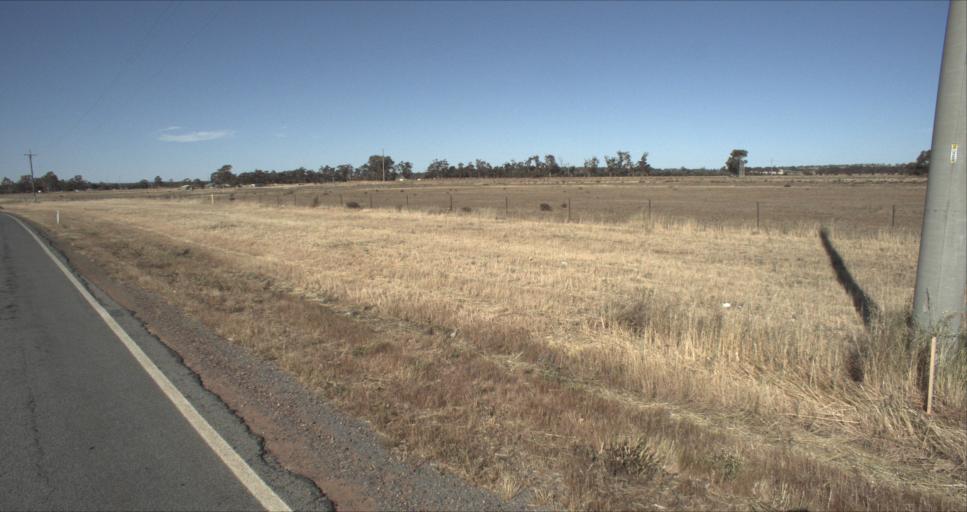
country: AU
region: New South Wales
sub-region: Leeton
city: Leeton
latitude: -34.6141
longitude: 146.4023
